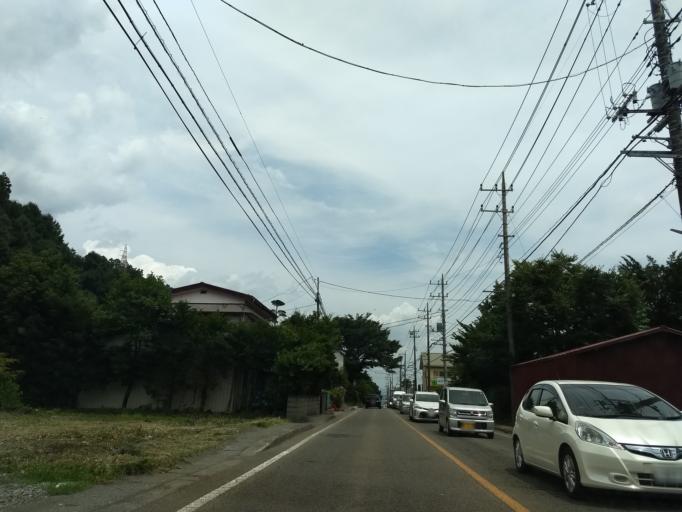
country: JP
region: Yamanashi
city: Fujikawaguchiko
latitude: 35.5055
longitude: 138.8217
